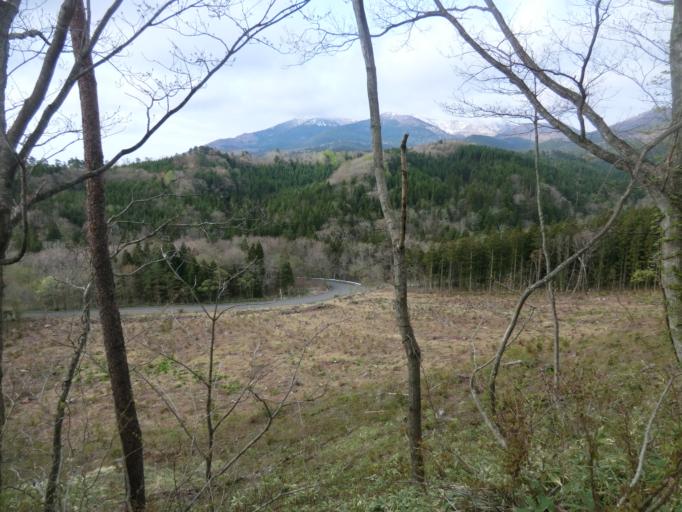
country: JP
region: Aomori
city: Mutsu
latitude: 41.3171
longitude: 141.1513
